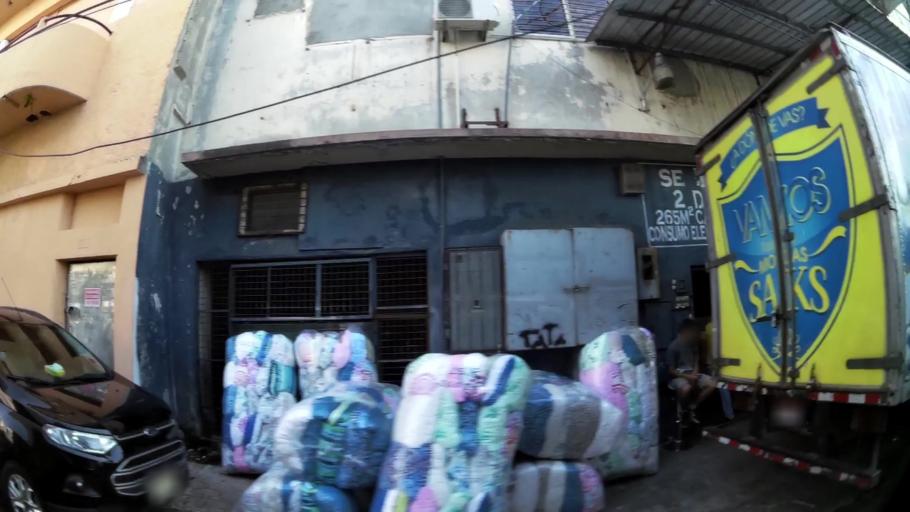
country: PA
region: Panama
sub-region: Distrito de Panama
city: Ancon
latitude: 8.9552
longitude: -79.5399
